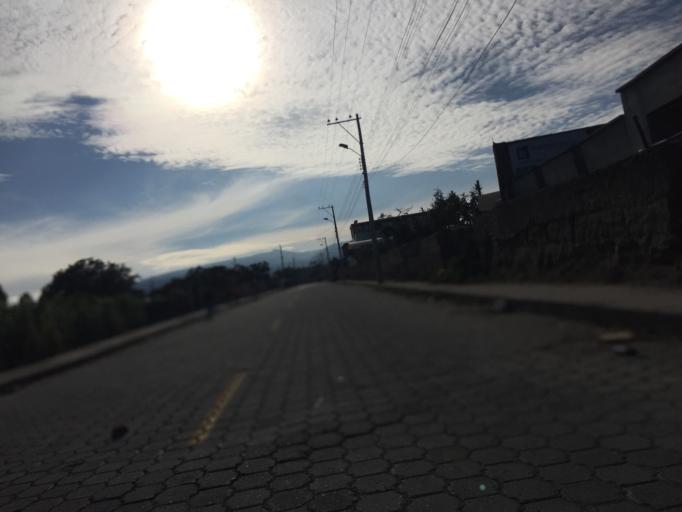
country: EC
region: Imbabura
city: Atuntaqui
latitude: 0.3378
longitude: -78.2011
